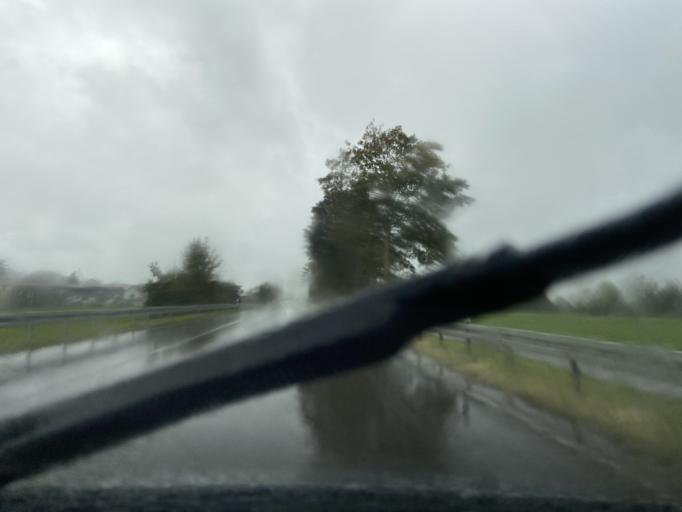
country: DE
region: Baden-Wuerttemberg
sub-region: Tuebingen Region
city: Mengen
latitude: 48.0552
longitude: 9.3314
